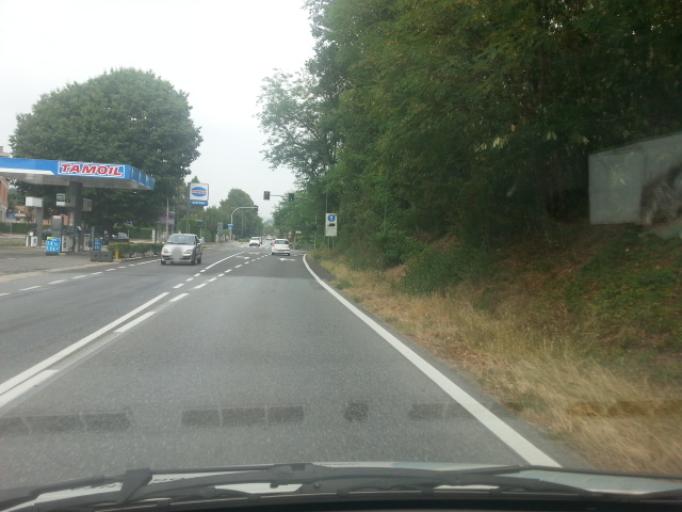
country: IT
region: Piedmont
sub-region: Provincia di Torino
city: Rivalta di Torino
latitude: 45.0336
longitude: 7.5253
